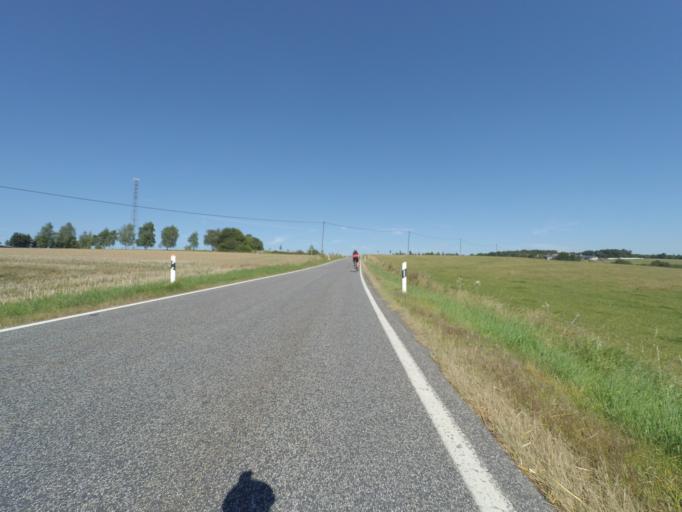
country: DE
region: Rheinland-Pfalz
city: Filz
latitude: 50.1589
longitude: 6.9874
